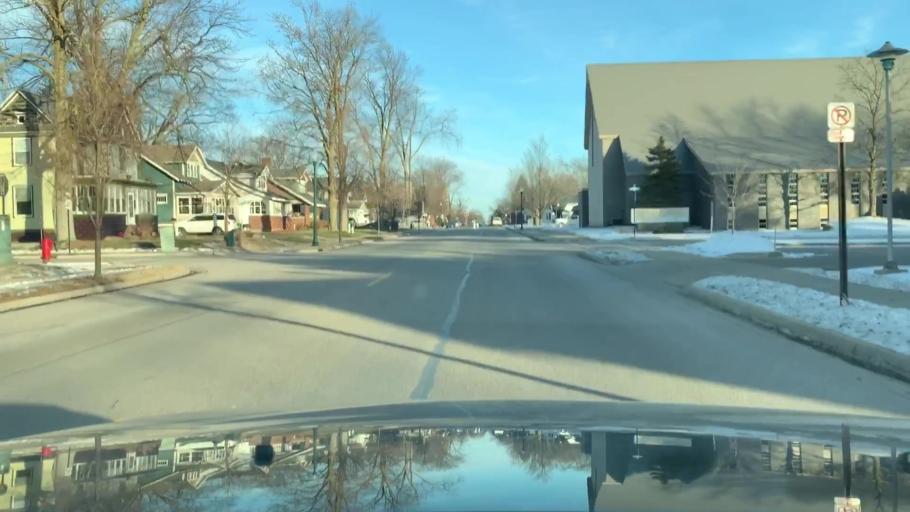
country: US
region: Michigan
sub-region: Ottawa County
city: Zeeland
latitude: 42.8123
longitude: -86.0266
